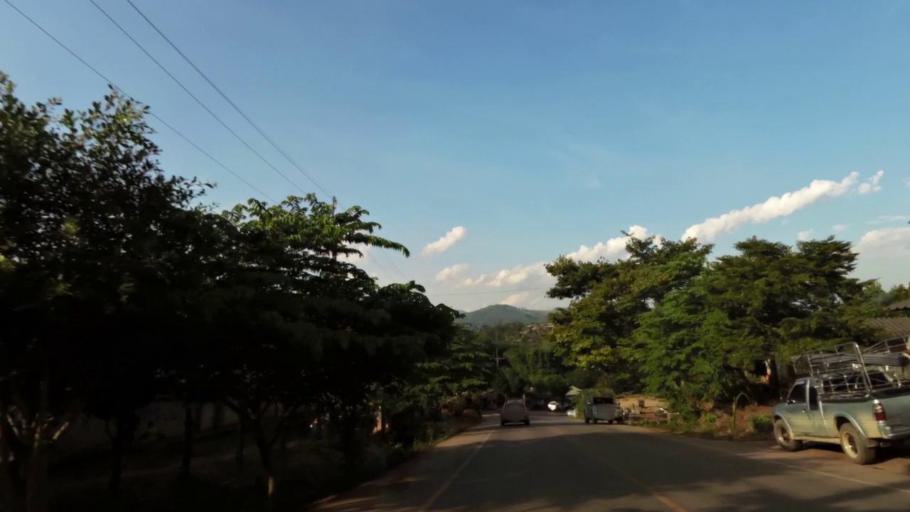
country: TH
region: Chiang Rai
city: Khun Tan
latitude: 19.8637
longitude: 100.3983
